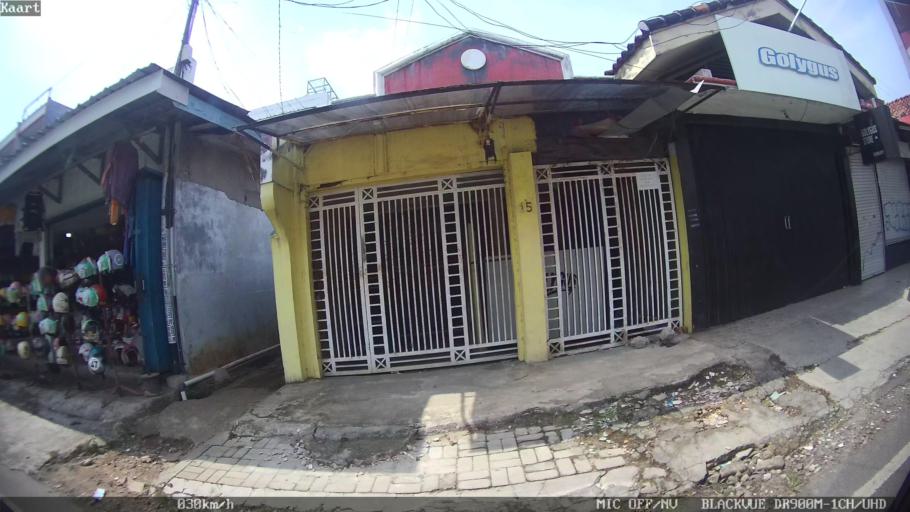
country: ID
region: Lampung
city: Kedaton
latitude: -5.3874
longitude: 105.2623
